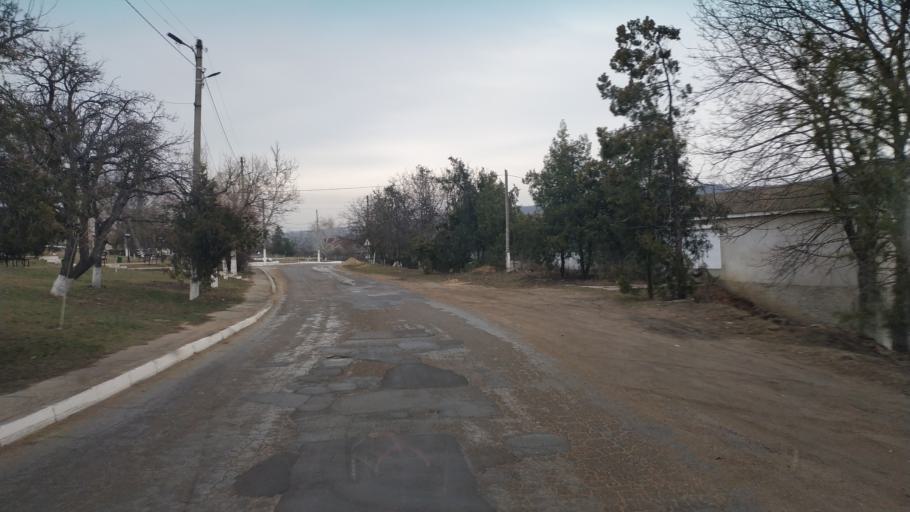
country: MD
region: Chisinau
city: Singera
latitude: 46.8270
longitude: 28.9738
